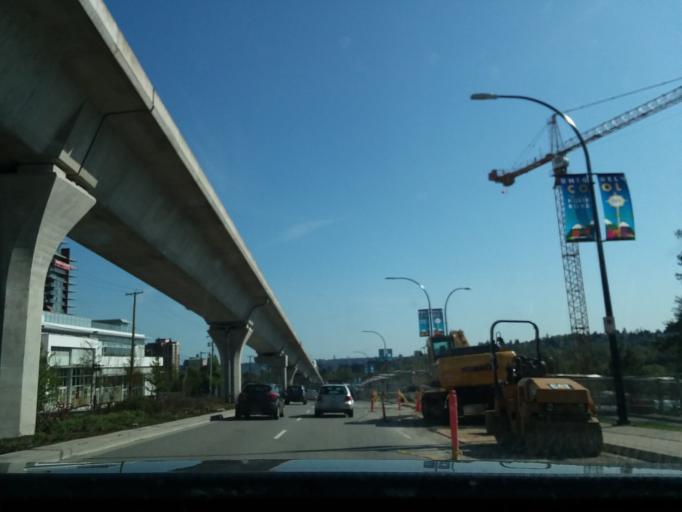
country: CA
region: British Columbia
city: New Westminster
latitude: 49.2512
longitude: -122.8931
